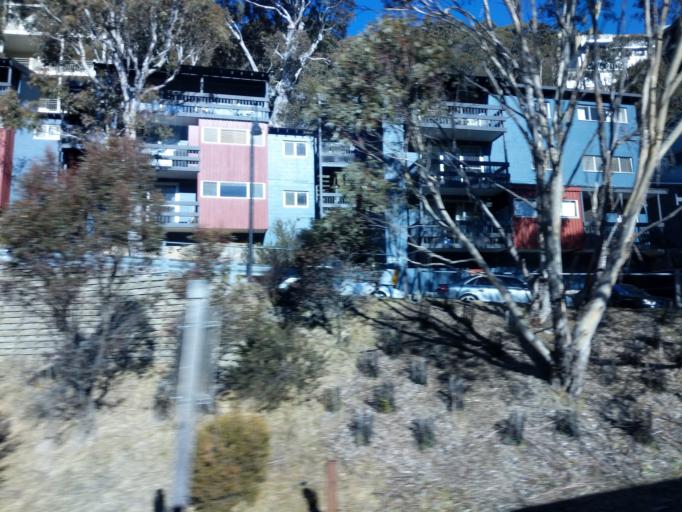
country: AU
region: New South Wales
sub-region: Snowy River
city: Jindabyne
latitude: -36.5030
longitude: 148.3086
